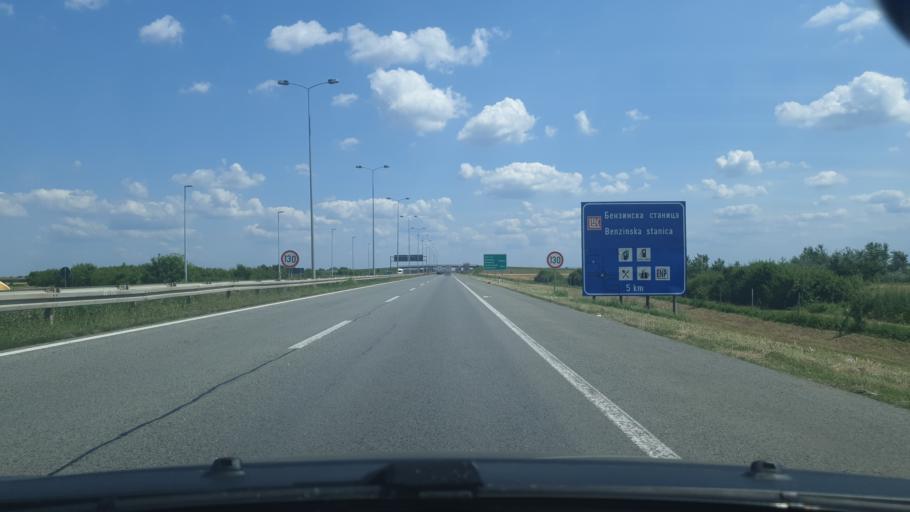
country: RS
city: Simanovci
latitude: 44.8731
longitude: 20.1323
